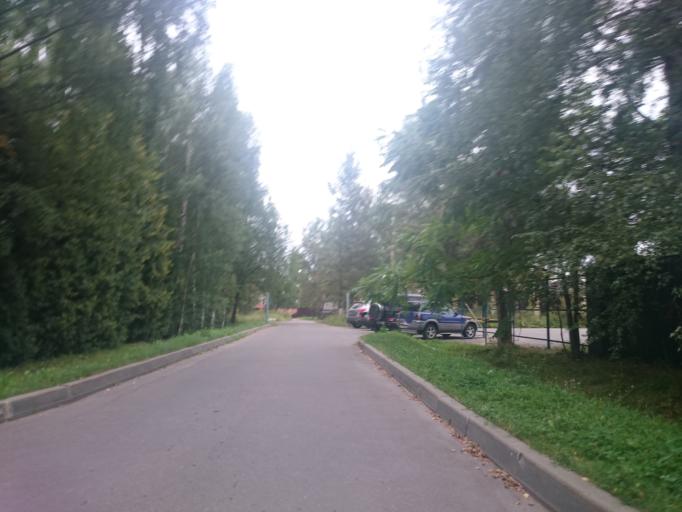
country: RU
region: Moskovskaya
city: Novopodrezkovo
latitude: 55.8954
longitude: 37.3557
